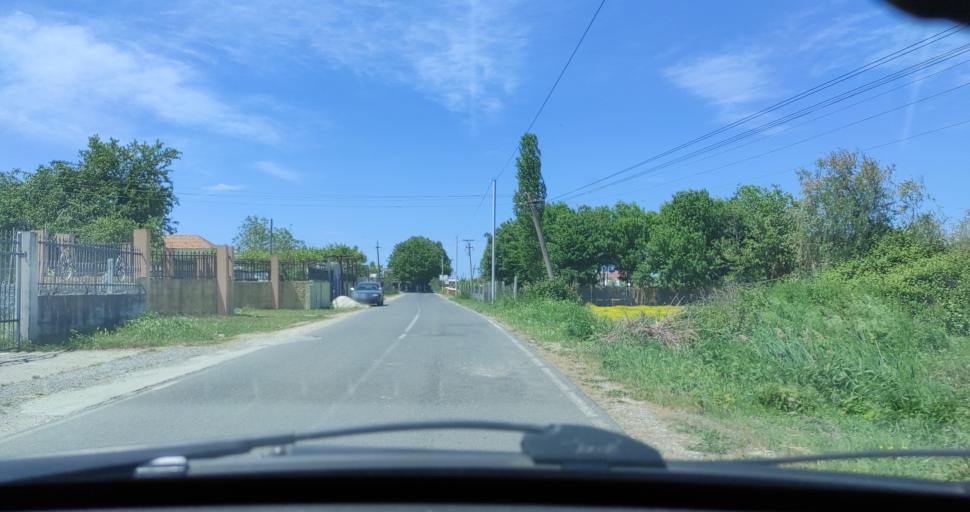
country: AL
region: Lezhe
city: Lezhe
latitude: 41.7564
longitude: 19.6184
